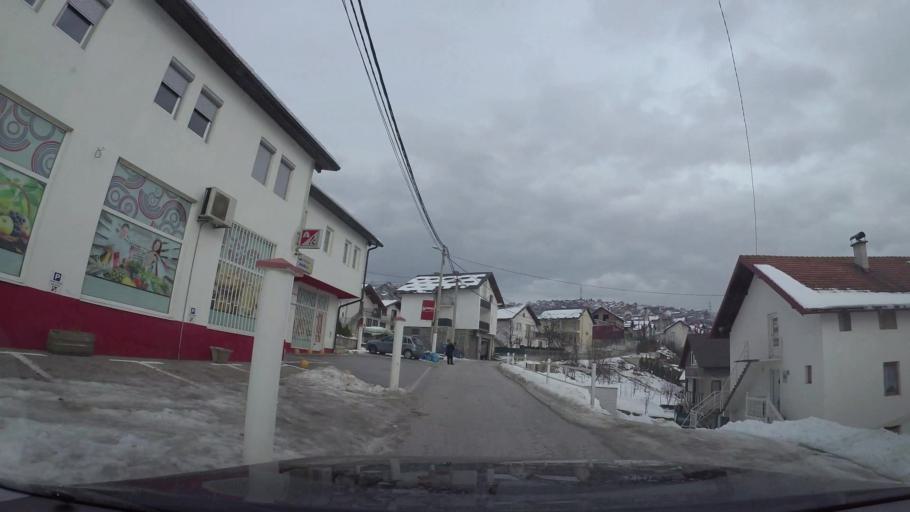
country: BA
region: Federation of Bosnia and Herzegovina
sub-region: Kanton Sarajevo
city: Sarajevo
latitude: 43.8588
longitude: 18.3269
